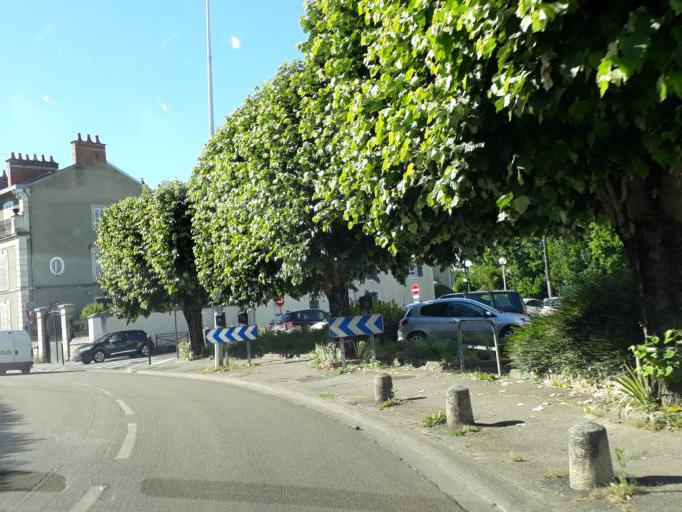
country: FR
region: Centre
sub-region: Departement du Cher
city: Bourges
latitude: 47.0847
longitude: 2.4027
